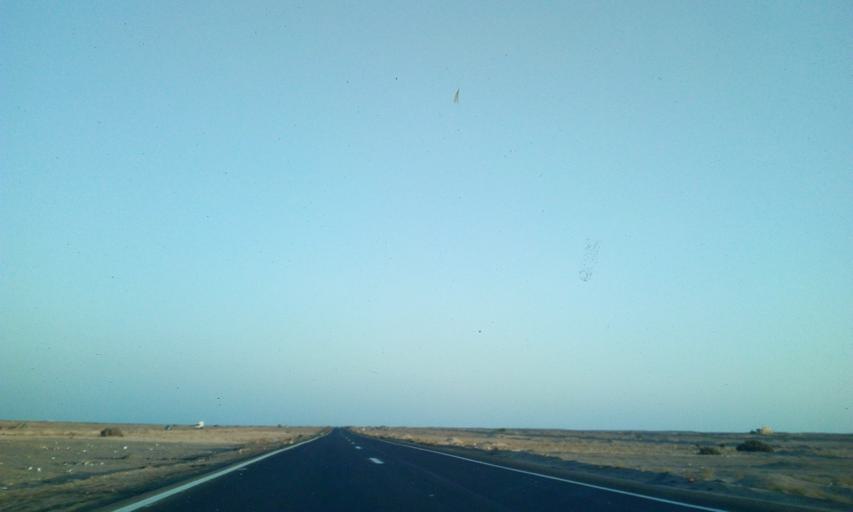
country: EG
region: South Sinai
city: Tor
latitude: 27.8138
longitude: 33.4601
